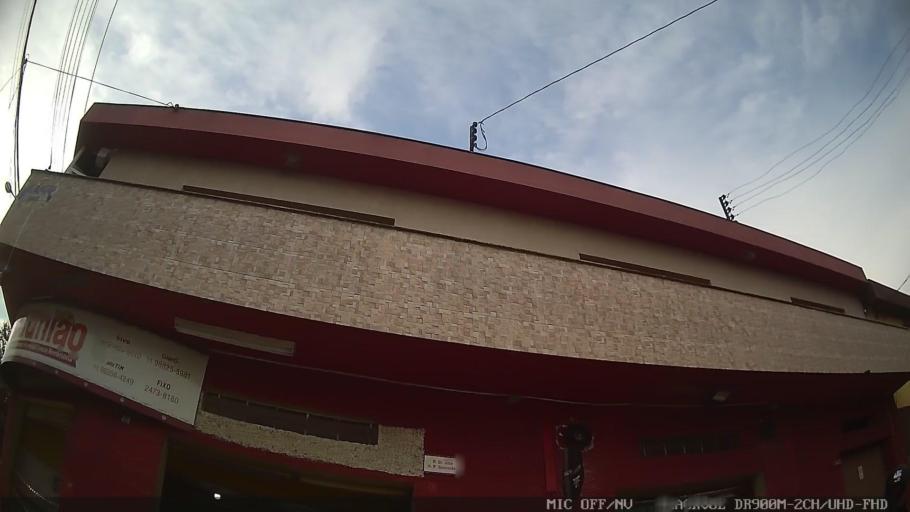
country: BR
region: Sao Paulo
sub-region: Braganca Paulista
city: Braganca Paulista
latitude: -22.9504
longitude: -46.5479
